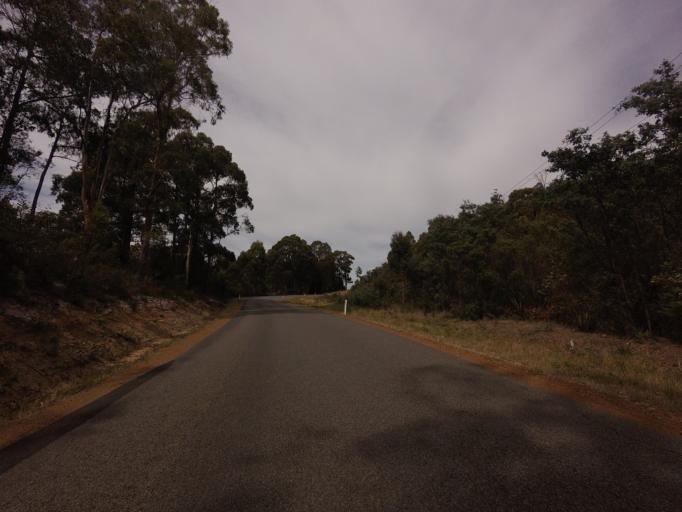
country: AU
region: Tasmania
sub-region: Sorell
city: Sorell
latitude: -42.5824
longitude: 147.5580
